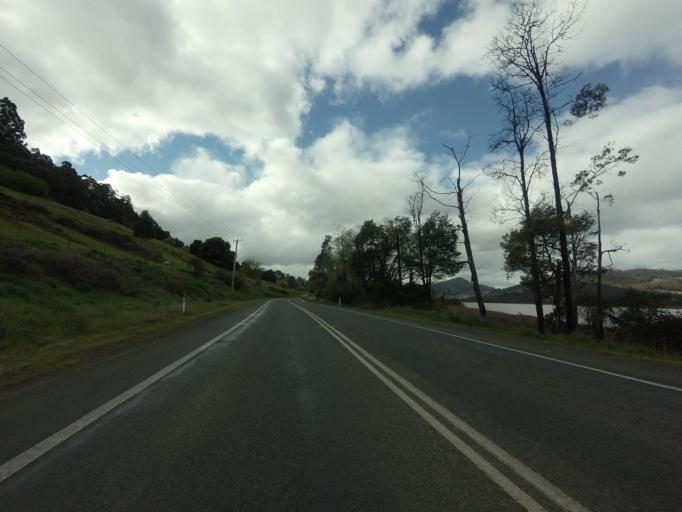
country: AU
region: Tasmania
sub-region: Huon Valley
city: Franklin
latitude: -43.1016
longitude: 147.0032
